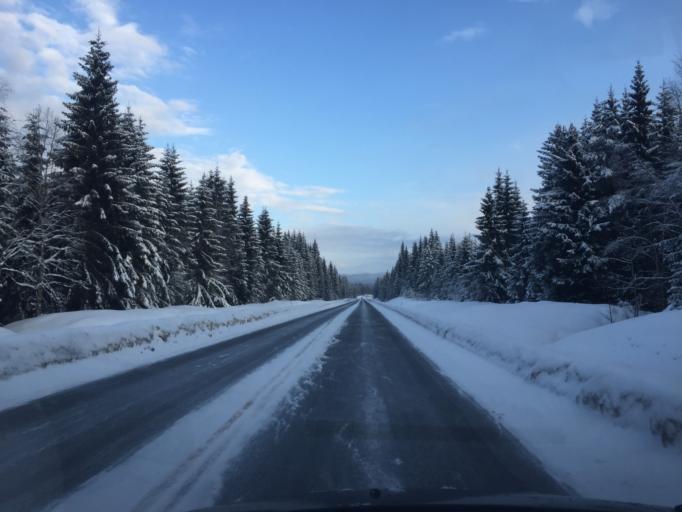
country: NO
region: Hedmark
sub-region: Trysil
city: Innbygda
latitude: 61.0771
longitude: 11.9766
